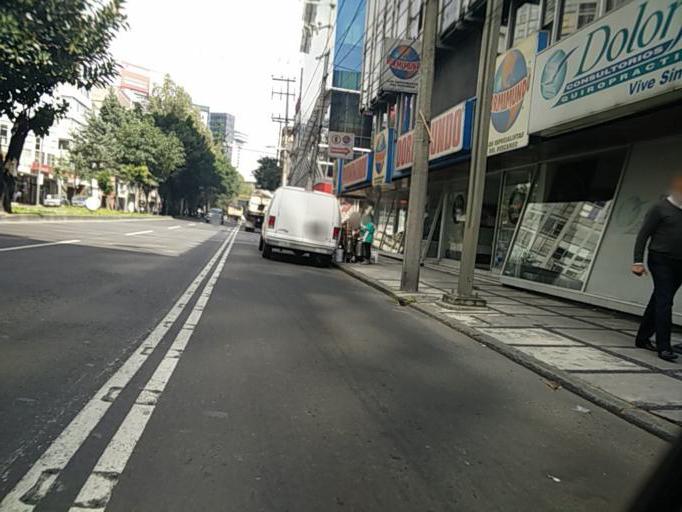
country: MX
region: Mexico City
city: Miguel Hidalgo
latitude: 19.4356
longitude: -99.1829
